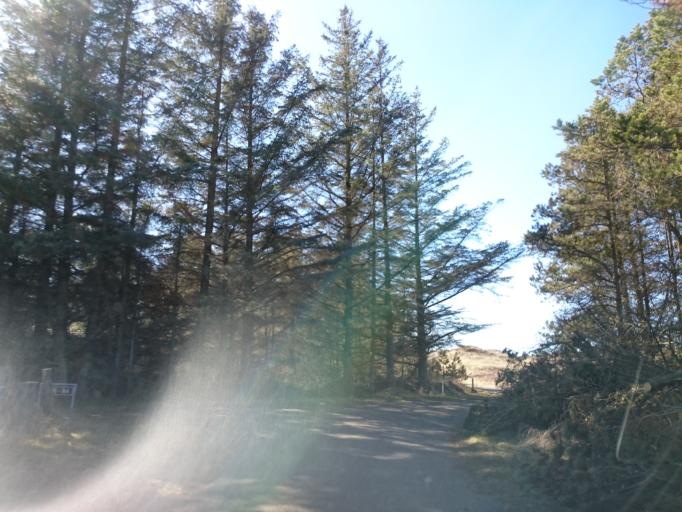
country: DK
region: North Denmark
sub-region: Frederikshavn Kommune
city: Skagen
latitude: 57.6726
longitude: 10.4963
